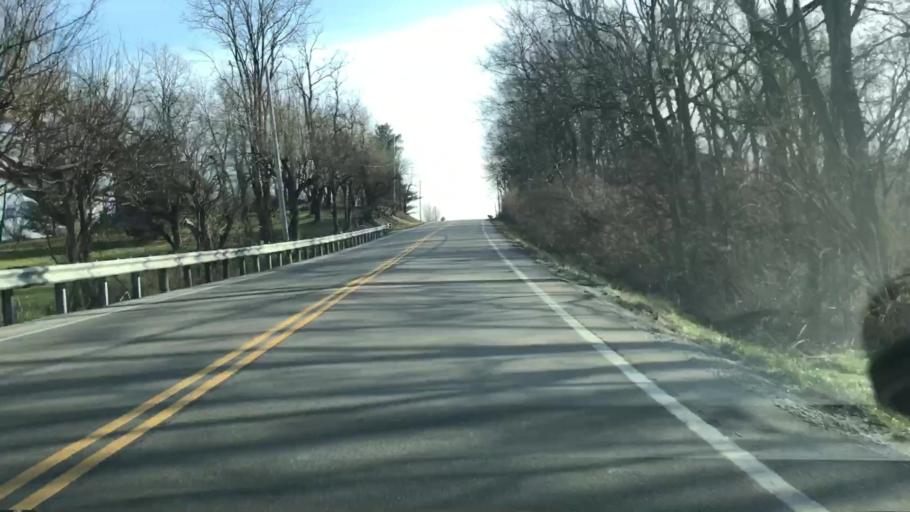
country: US
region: Ohio
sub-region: Greene County
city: Fairborn
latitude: 39.8114
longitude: -83.9808
